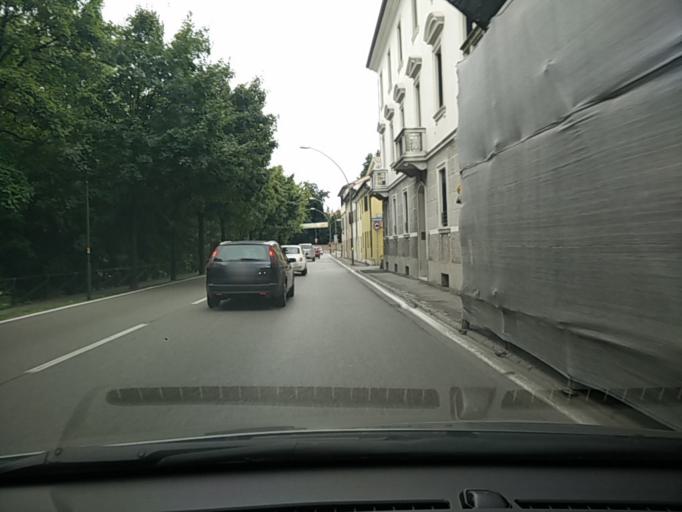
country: IT
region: Veneto
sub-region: Provincia di Treviso
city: Treviso
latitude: 45.6663
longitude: 12.2346
